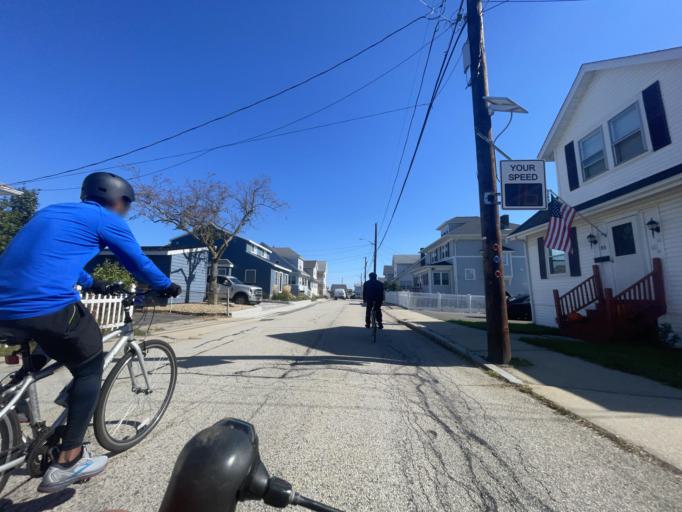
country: US
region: Massachusetts
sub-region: Norfolk County
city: Quincy
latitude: 42.2811
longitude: -71.0211
